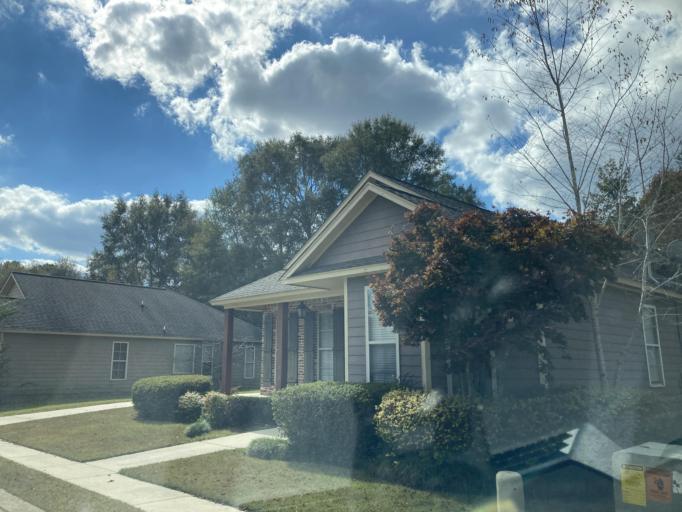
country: US
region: Mississippi
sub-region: Lamar County
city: Arnold Line
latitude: 31.3369
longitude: -89.3727
